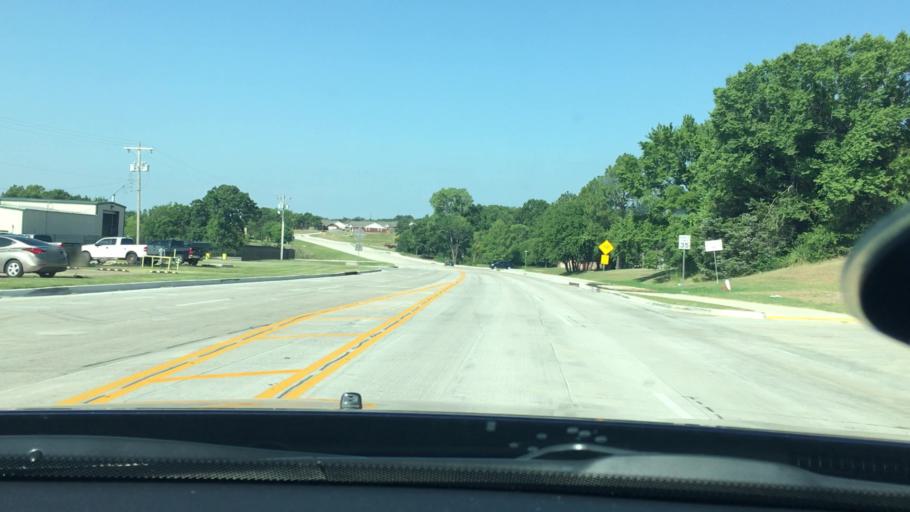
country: US
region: Oklahoma
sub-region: Pontotoc County
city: Ada
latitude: 34.7619
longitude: -96.6649
